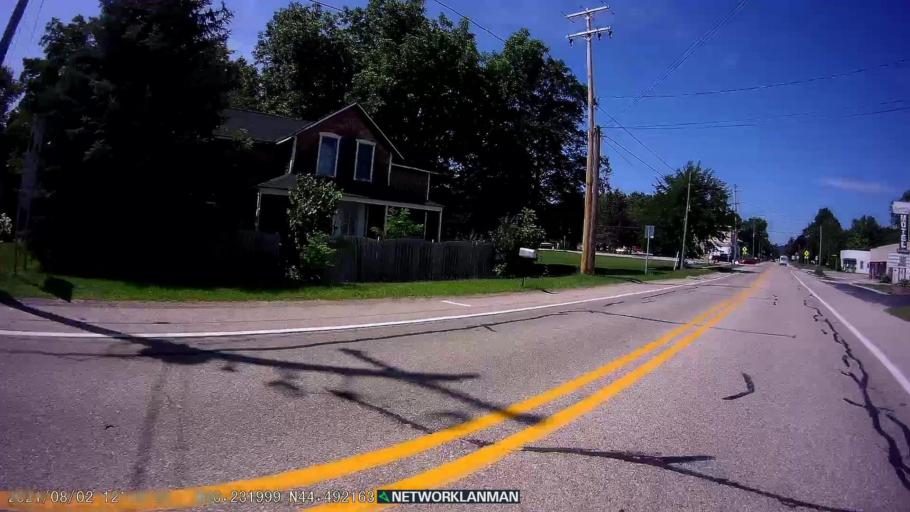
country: US
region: Michigan
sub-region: Benzie County
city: Frankfort
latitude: 44.4924
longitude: -86.2317
